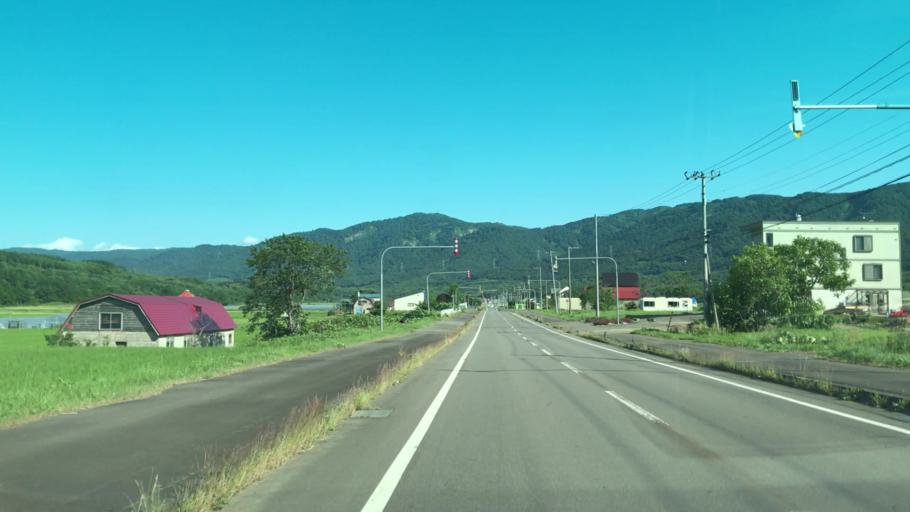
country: JP
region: Hokkaido
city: Yoichi
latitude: 43.0529
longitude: 140.7203
